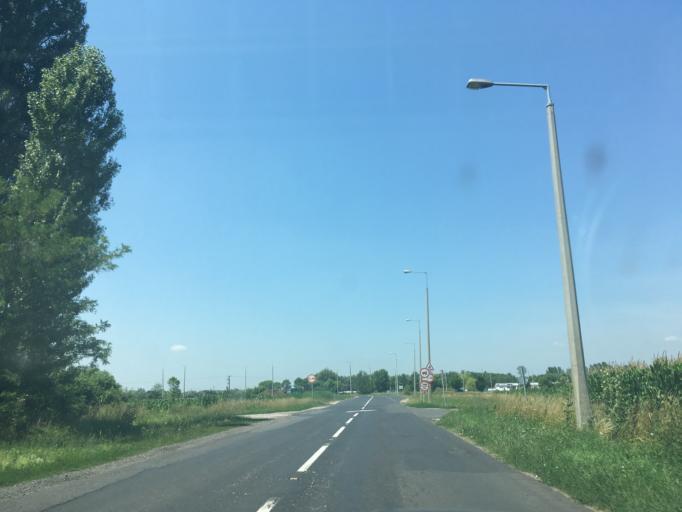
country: HU
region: Hajdu-Bihar
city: Mikepercs
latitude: 47.4842
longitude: 21.6361
